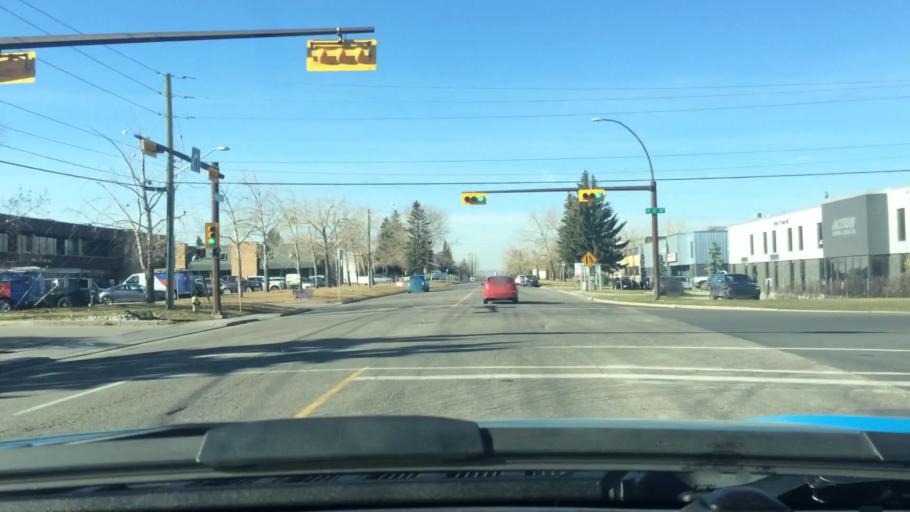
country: CA
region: Alberta
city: Calgary
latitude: 51.0769
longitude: -114.0113
